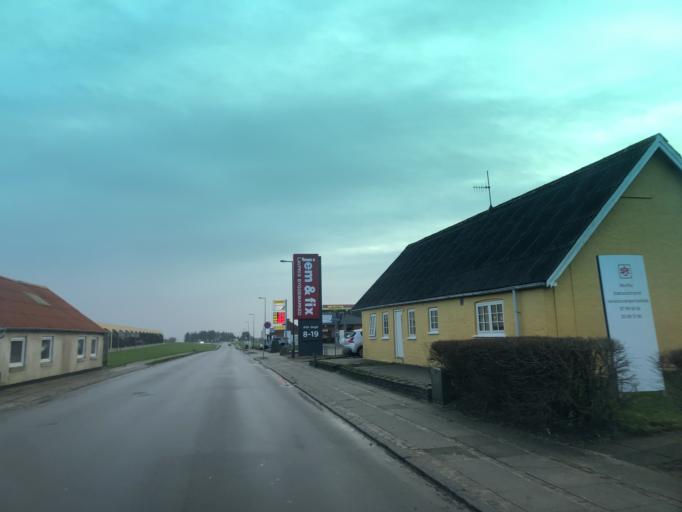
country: DK
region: North Denmark
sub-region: Thisted Kommune
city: Hurup
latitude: 56.7457
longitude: 8.4320
